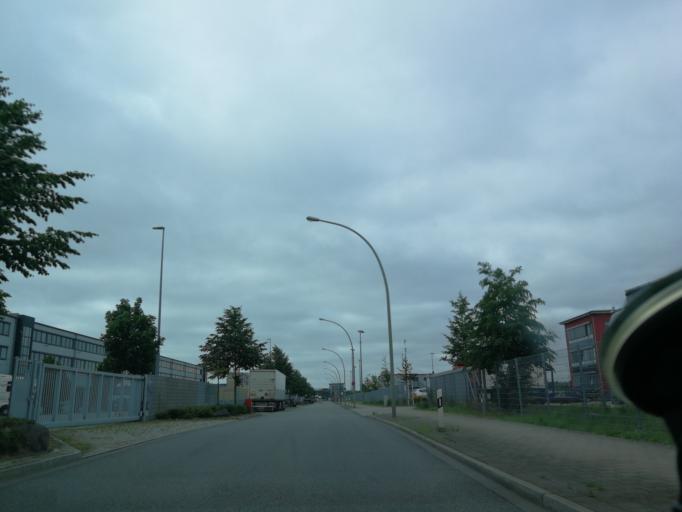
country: DE
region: Hamburg
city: Altona
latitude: 53.5057
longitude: 9.9217
